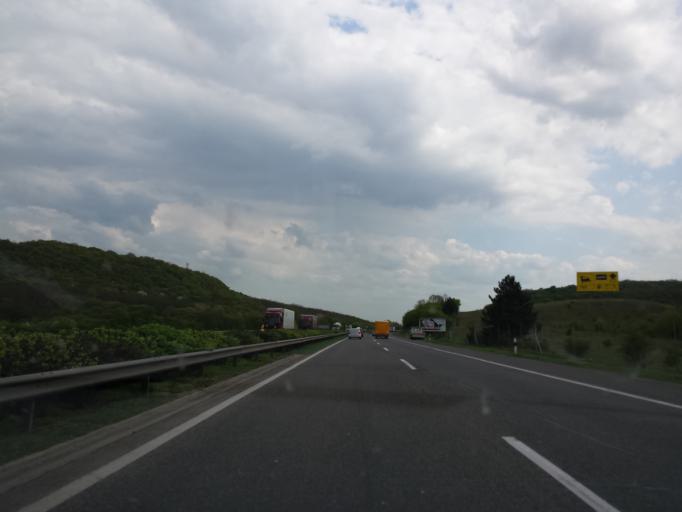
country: HU
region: Fejer
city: Szarliget
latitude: 47.5562
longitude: 18.4868
